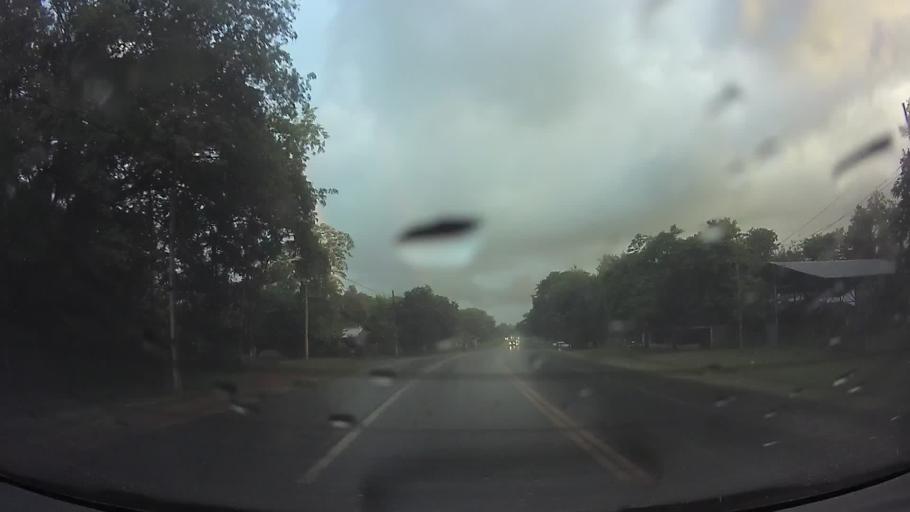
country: PY
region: Paraguari
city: Paraguari
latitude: -25.5938
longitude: -57.2189
